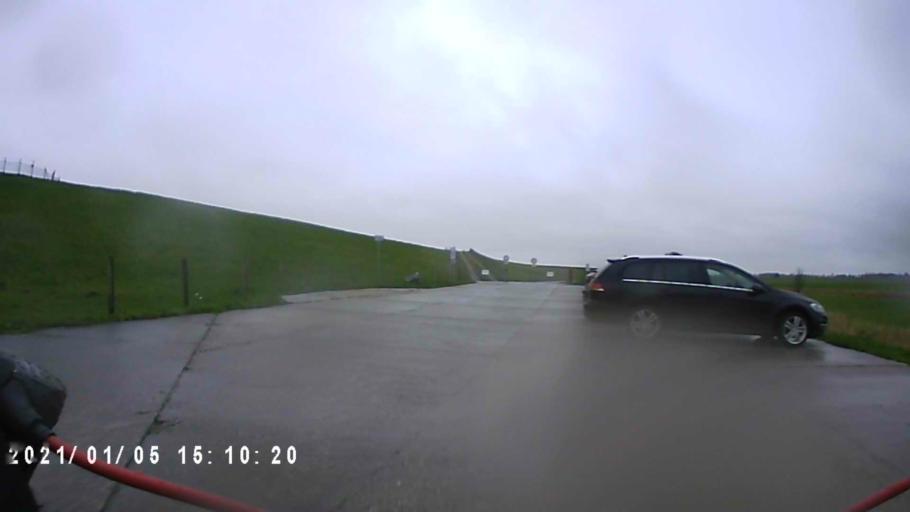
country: DE
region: Lower Saxony
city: Bunde
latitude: 53.2324
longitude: 7.2117
